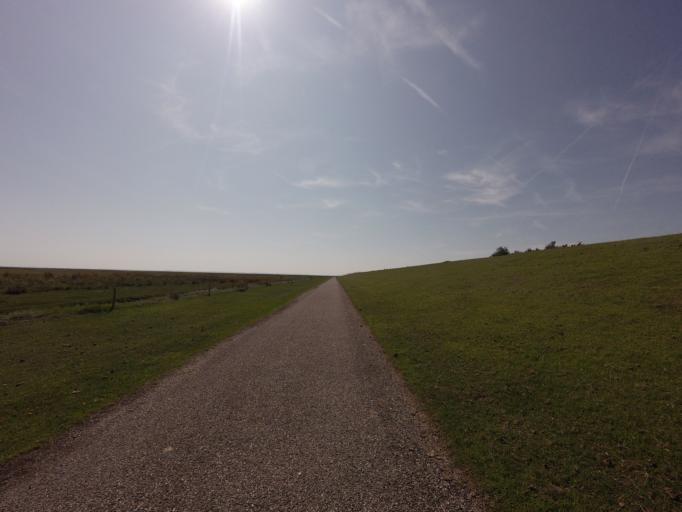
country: NL
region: Friesland
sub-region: Gemeente Schiermonnikoog
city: Schiermonnikoog
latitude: 53.4787
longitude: 6.2105
